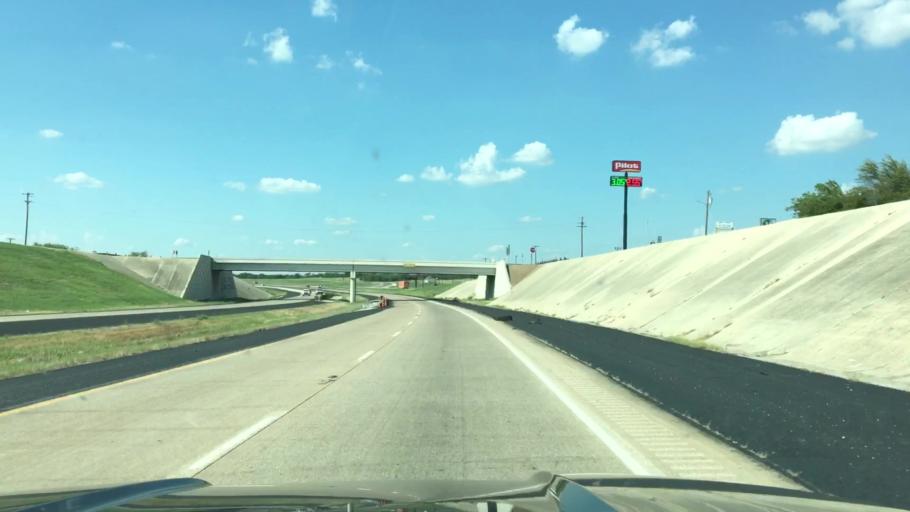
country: US
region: Texas
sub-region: Wise County
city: New Fairview
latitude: 33.0984
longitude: -97.4709
